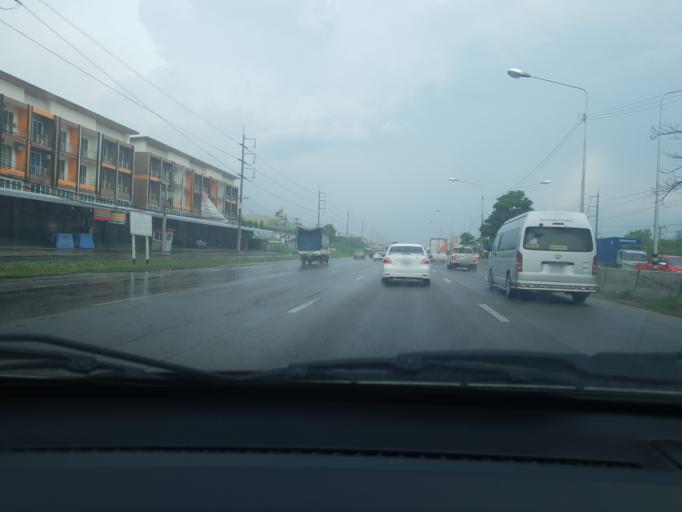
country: TH
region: Samut Sakhon
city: Samut Sakhon
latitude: 13.5287
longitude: 100.1976
